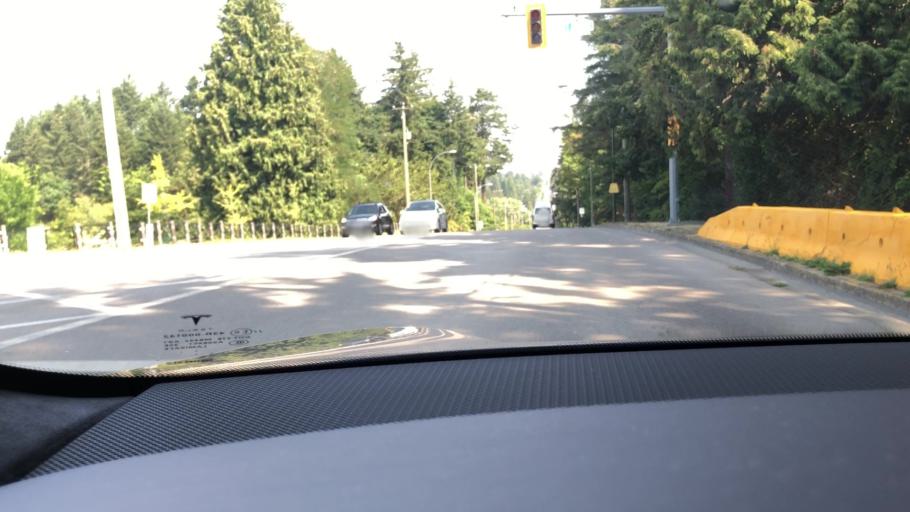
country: US
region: Washington
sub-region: Whatcom County
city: Point Roberts
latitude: 49.0043
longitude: -123.0686
